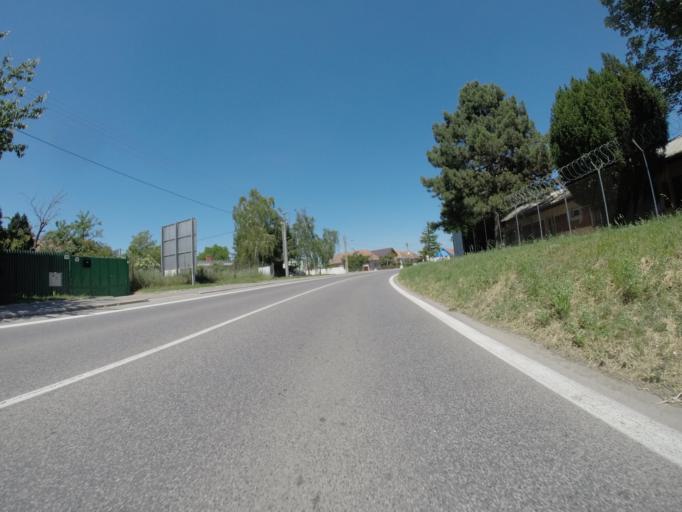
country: SK
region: Trnavsky
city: Hlohovec
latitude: 48.4393
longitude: 17.8045
